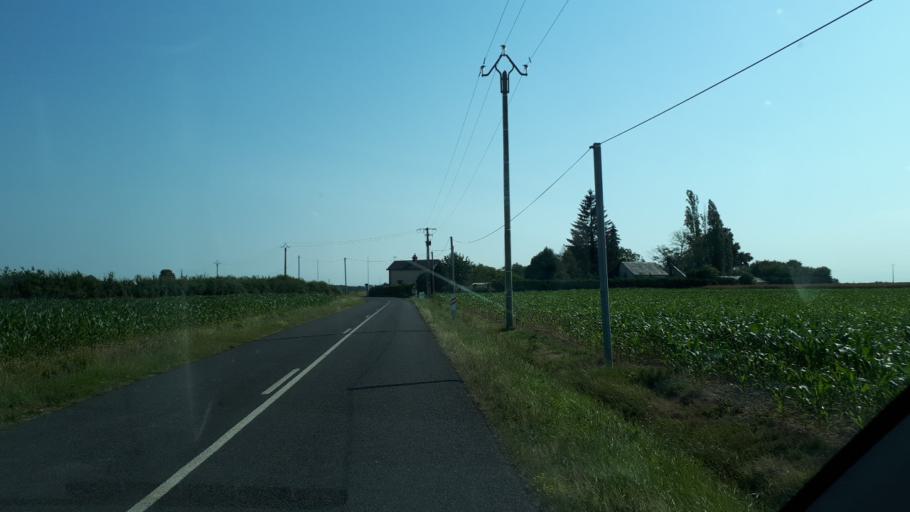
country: FR
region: Centre
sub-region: Departement du Loir-et-Cher
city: Droue
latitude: 48.0567
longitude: 1.1034
